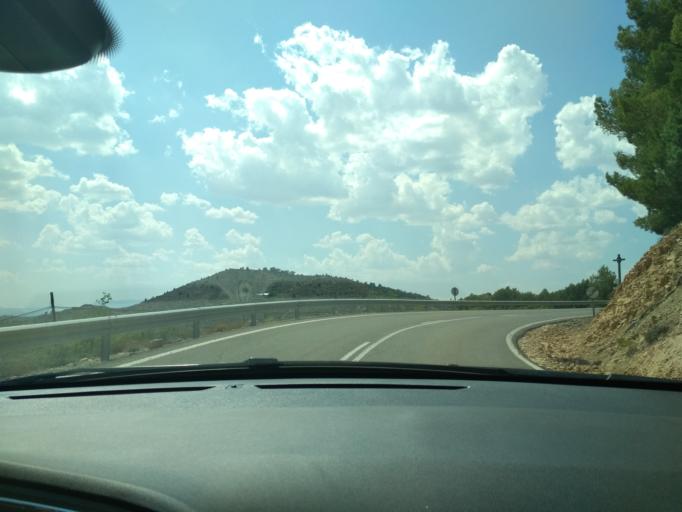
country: ES
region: Aragon
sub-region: Provincia de Teruel
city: Rubielos de Mora
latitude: 40.1860
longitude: -0.6480
